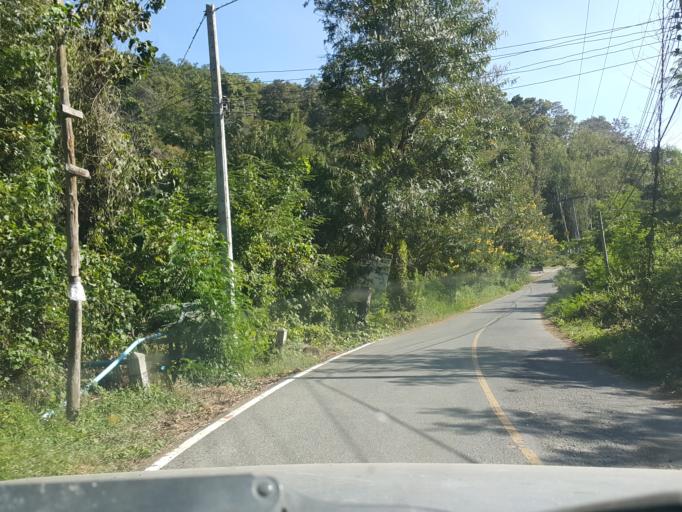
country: TH
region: Mae Hong Son
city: Mae Hi
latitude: 19.3073
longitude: 98.4676
